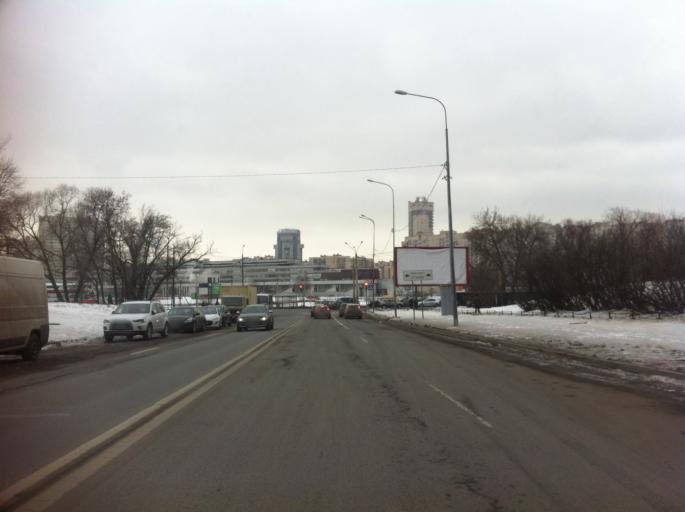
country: RU
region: St.-Petersburg
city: Dachnoye
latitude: 59.8476
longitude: 30.2287
